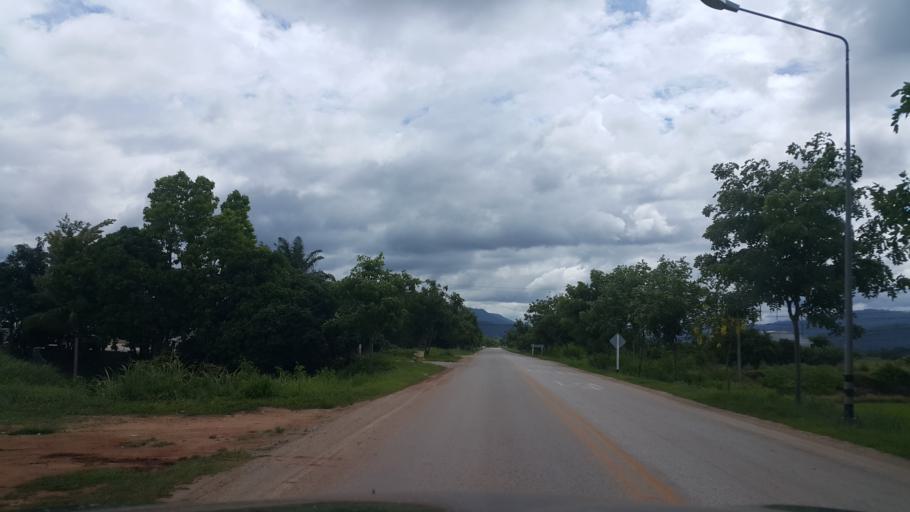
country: TH
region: Phitsanulok
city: Chat Trakan
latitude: 17.2710
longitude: 100.6093
